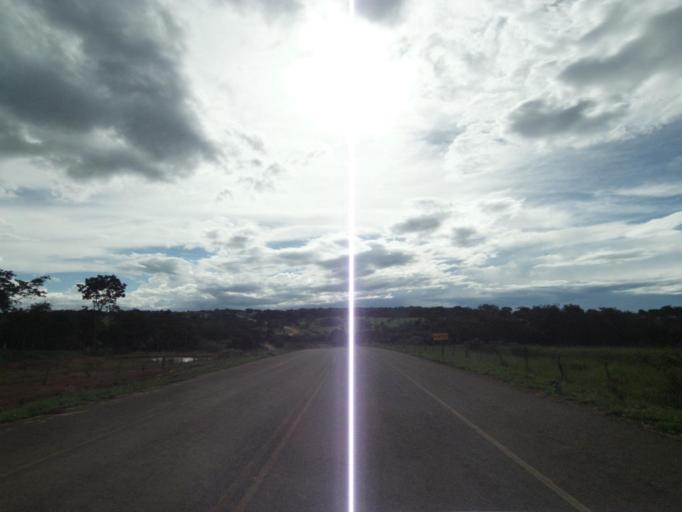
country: BR
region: Goias
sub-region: Jaragua
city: Jaragua
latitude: -15.8420
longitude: -49.3564
